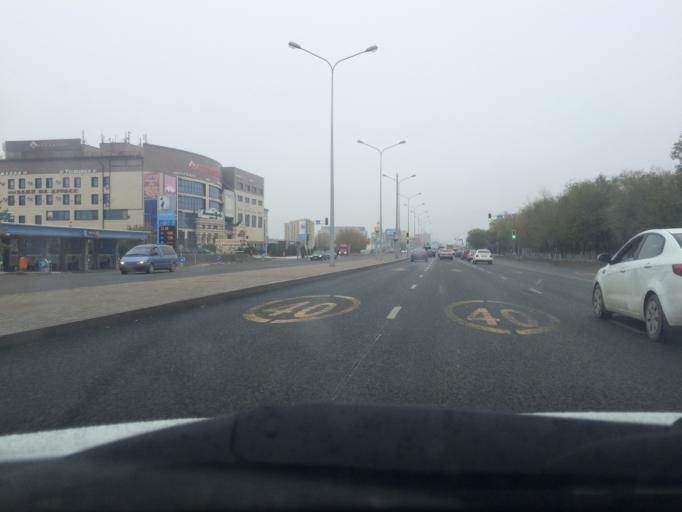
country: KZ
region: Astana Qalasy
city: Astana
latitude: 51.1753
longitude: 71.4008
